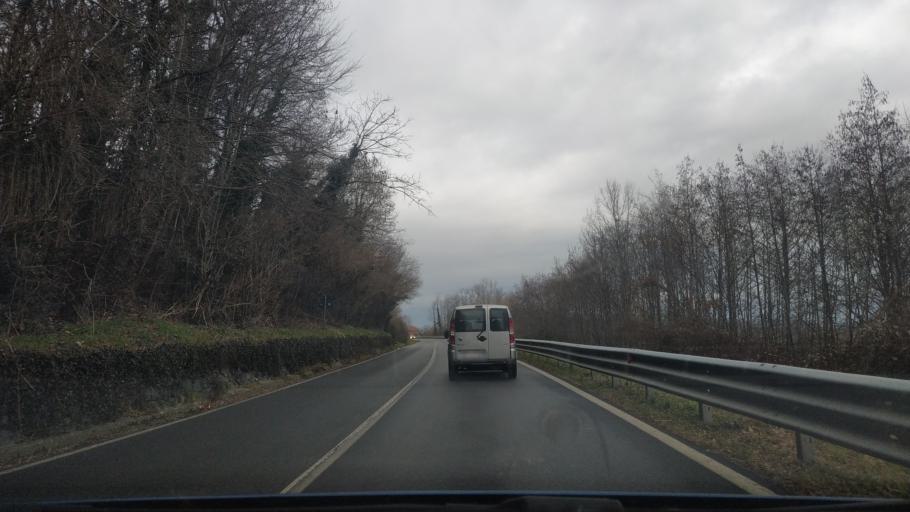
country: IT
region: Piedmont
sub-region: Provincia di Torino
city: Mercenasco
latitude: 45.3562
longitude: 7.8845
